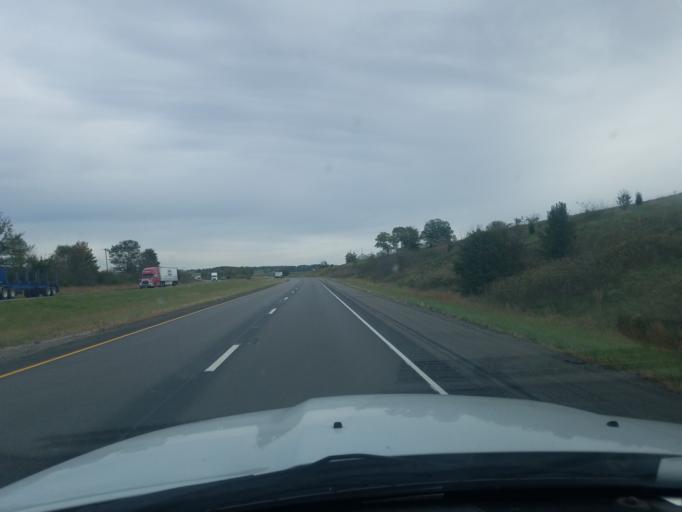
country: US
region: Indiana
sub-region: Dubois County
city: Ferdinand
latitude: 38.1994
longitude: -86.9206
